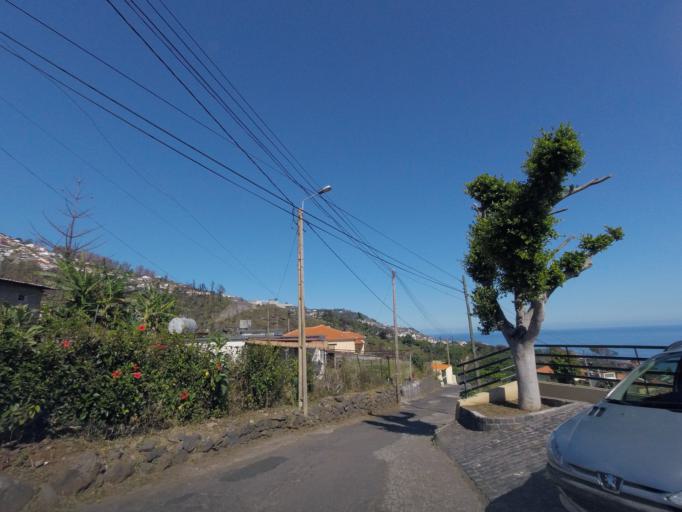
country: PT
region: Madeira
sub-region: Funchal
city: Nossa Senhora do Monte
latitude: 32.6644
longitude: -16.9002
